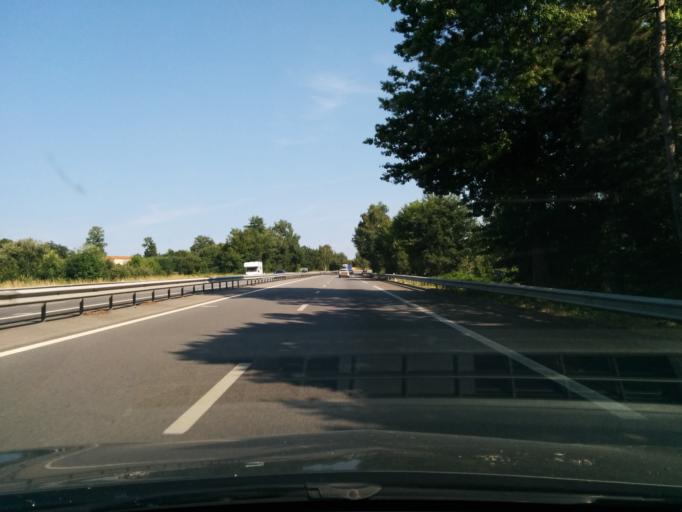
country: FR
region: Limousin
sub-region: Departement de la Haute-Vienne
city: Boisseuil
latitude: 45.7668
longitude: 1.3240
